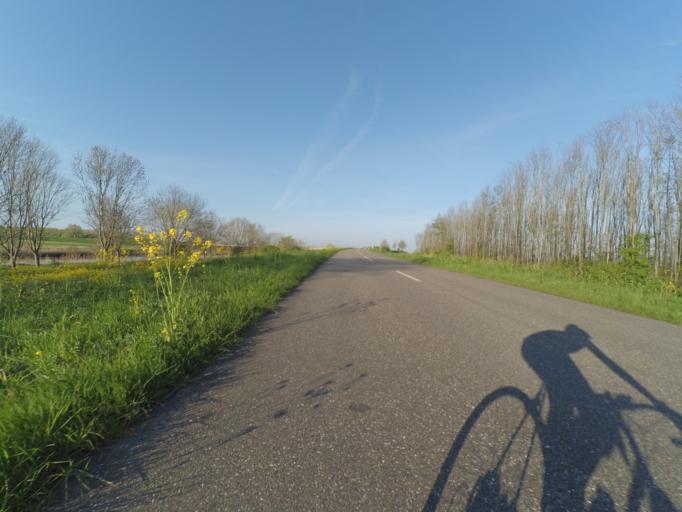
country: NL
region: Flevoland
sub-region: Gemeente Lelystad
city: Lelystad
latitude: 52.4287
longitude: 5.3988
